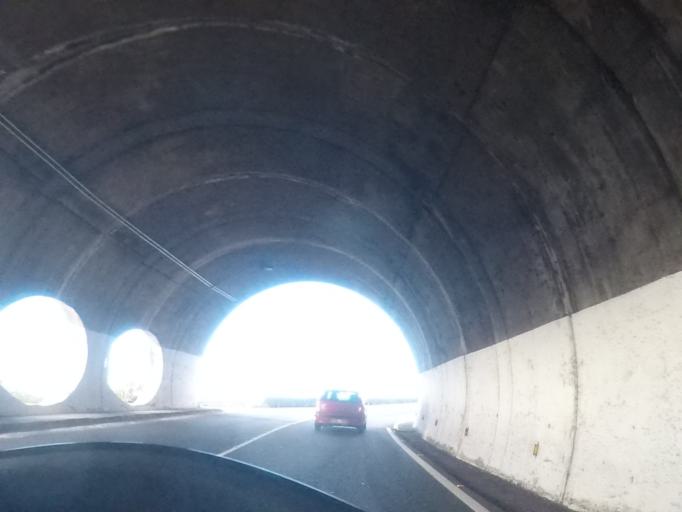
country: ES
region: Canary Islands
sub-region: Provincia de Santa Cruz de Tenerife
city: Garachico
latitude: 28.3721
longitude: -16.7471
